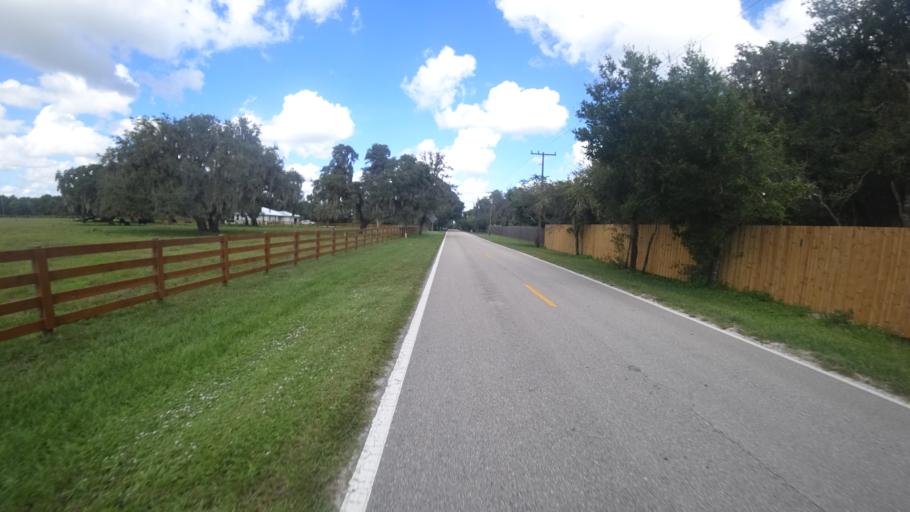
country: US
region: Florida
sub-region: Sarasota County
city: Lake Sarasota
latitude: 27.3139
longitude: -82.2670
